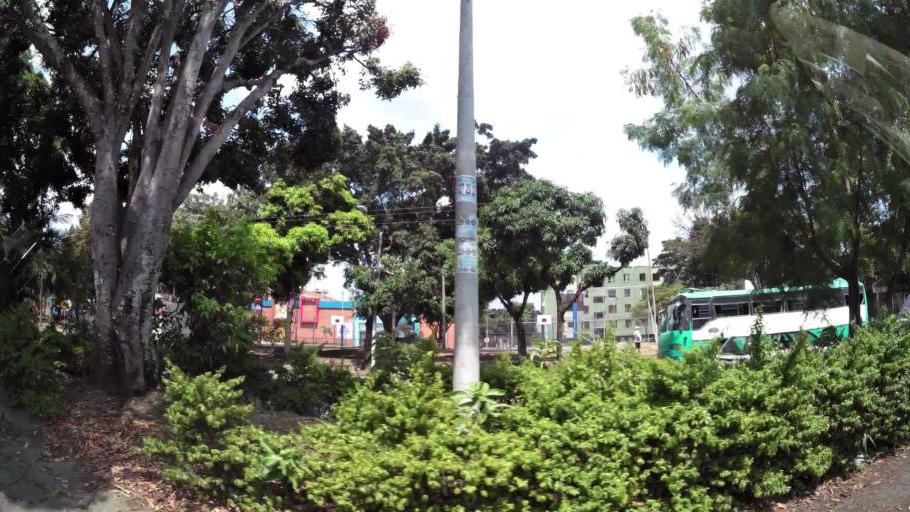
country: CO
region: Valle del Cauca
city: Cali
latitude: 3.4635
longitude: -76.5031
